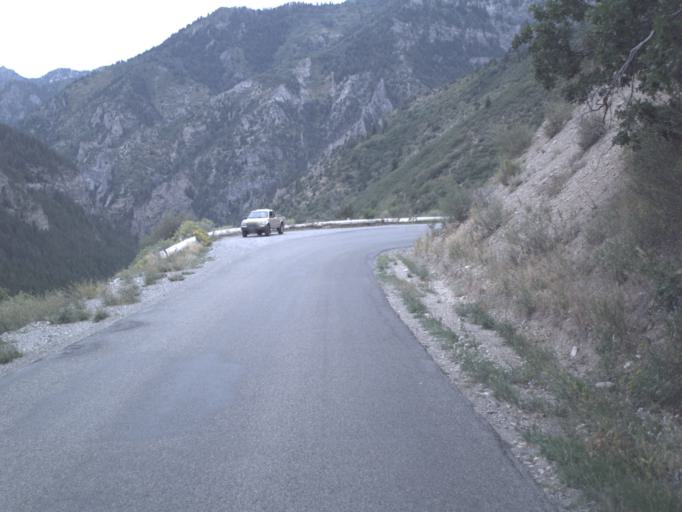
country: US
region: Utah
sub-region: Utah County
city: Cedar Hills
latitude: 40.4479
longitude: -111.6407
